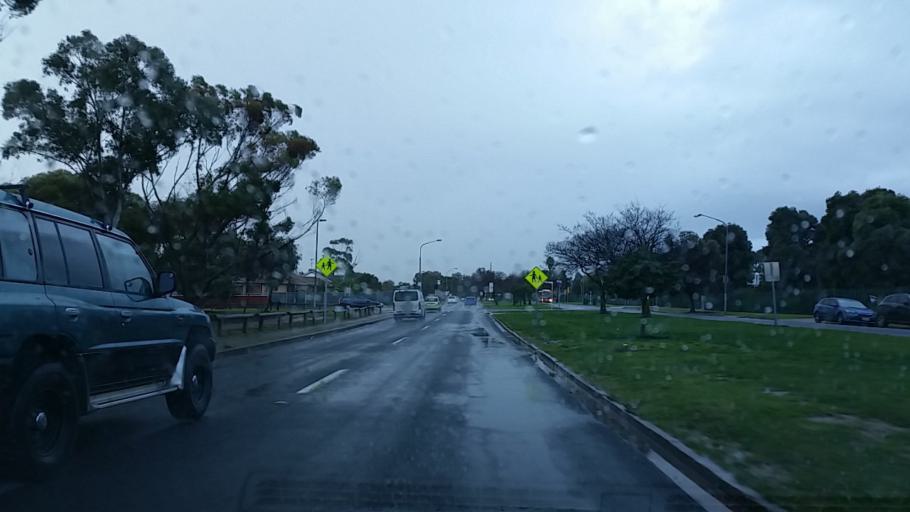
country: AU
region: South Australia
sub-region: Salisbury
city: Elizabeth
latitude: -34.7165
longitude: 138.6803
